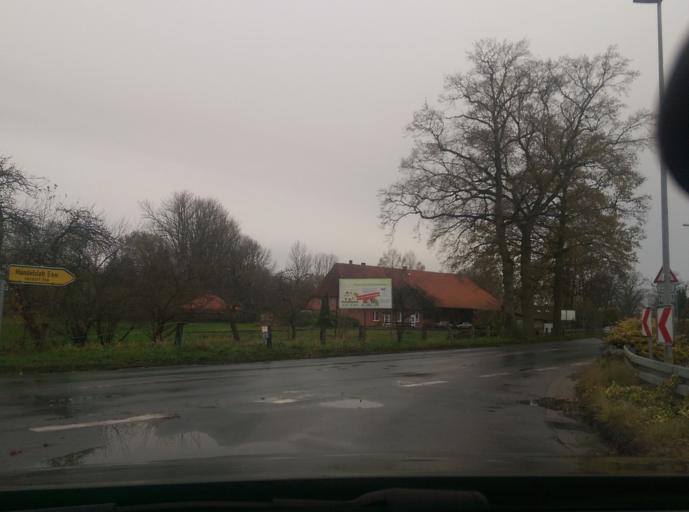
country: DE
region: Lower Saxony
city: Lindwedel
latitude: 52.5684
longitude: 9.6181
